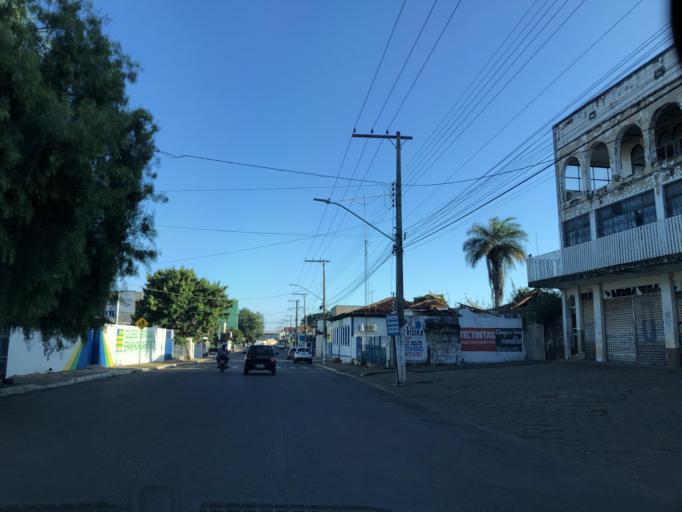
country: BR
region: Goias
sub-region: Luziania
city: Luziania
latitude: -16.2555
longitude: -47.9511
